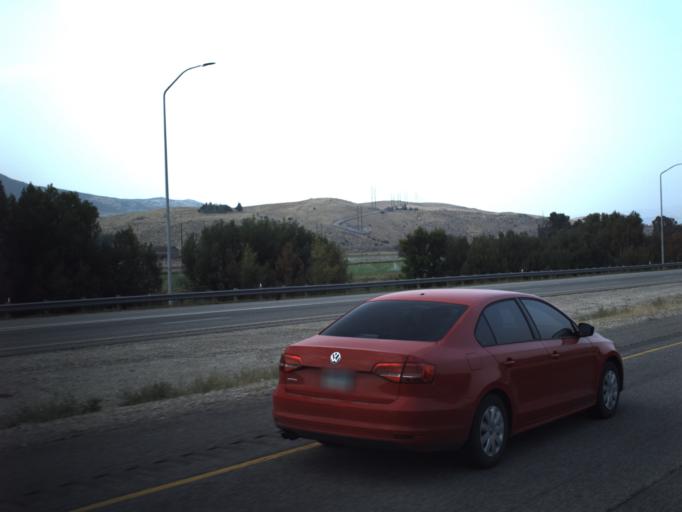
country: US
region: Utah
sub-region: Summit County
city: Coalville
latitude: 40.8151
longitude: -111.3996
